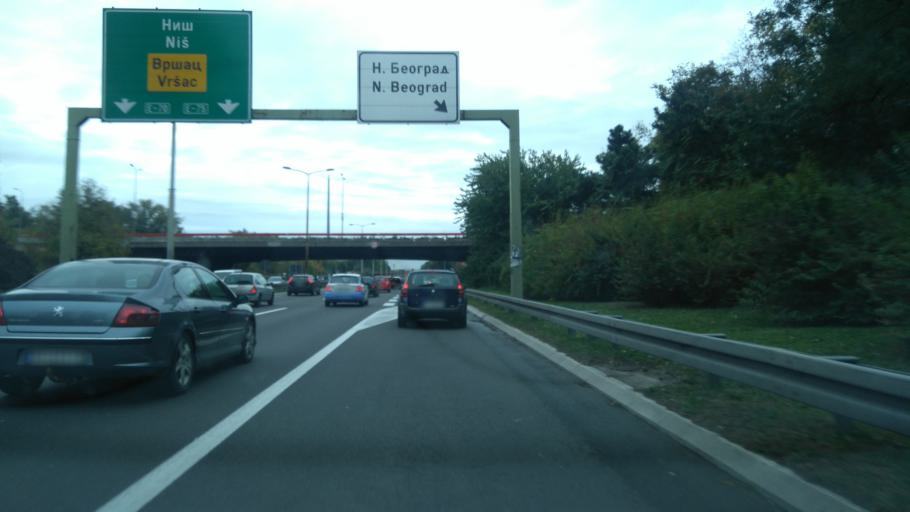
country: RS
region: Central Serbia
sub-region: Belgrade
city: Novi Beograd
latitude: 44.8187
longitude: 20.4064
